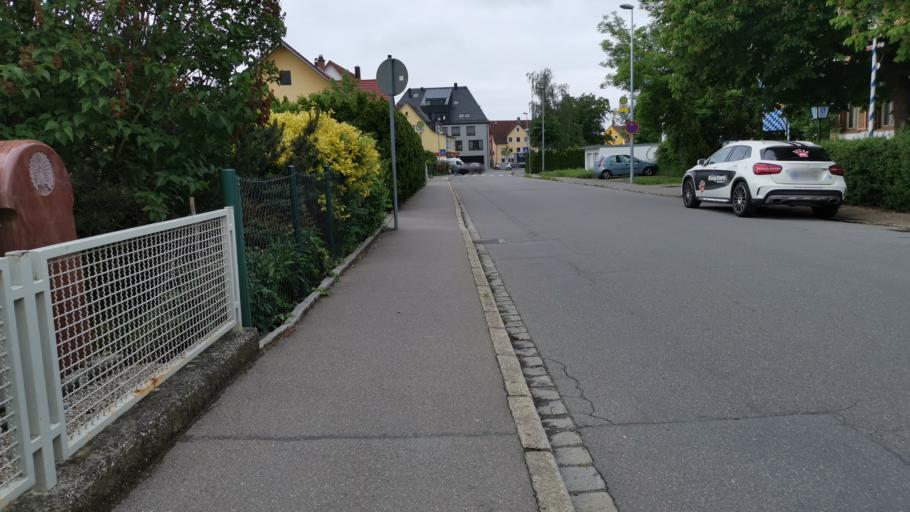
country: DE
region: Baden-Wuerttemberg
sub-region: Tuebingen Region
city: Immenstaad am Bodensee
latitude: 47.6718
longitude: 9.4132
